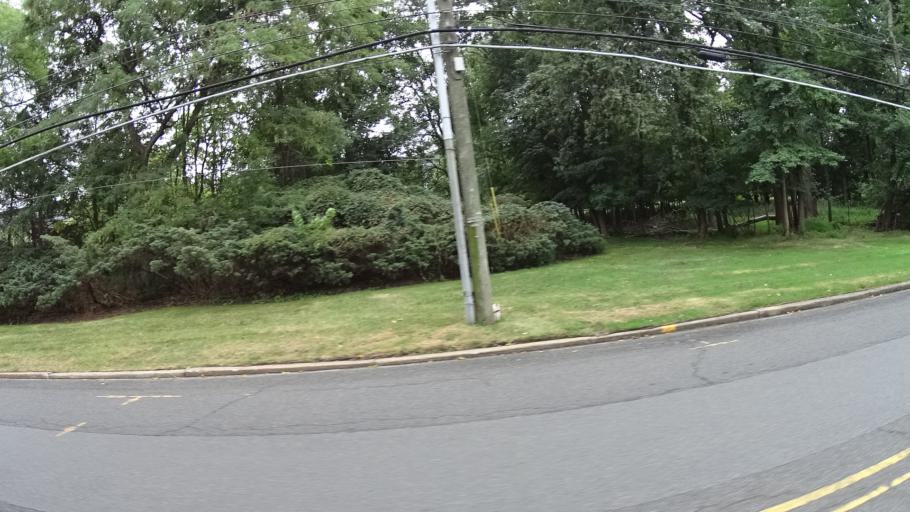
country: US
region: New Jersey
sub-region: Union County
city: New Providence
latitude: 40.6889
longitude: -74.3943
